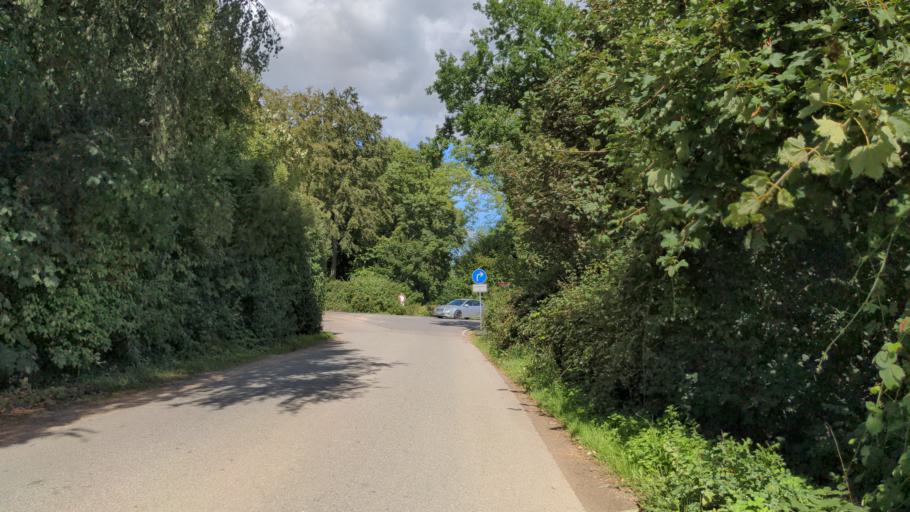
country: DE
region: Schleswig-Holstein
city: Beschendorf
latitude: 54.1999
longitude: 10.8230
